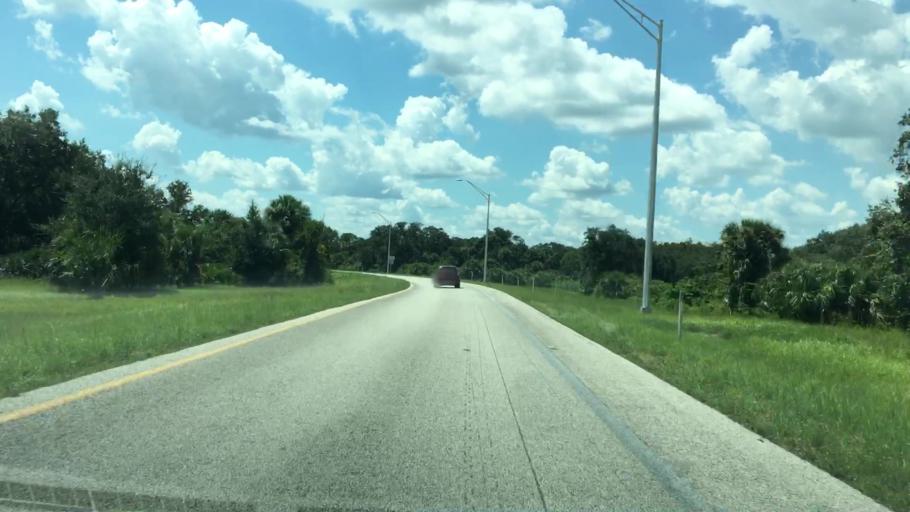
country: US
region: Florida
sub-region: Brevard County
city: South Patrick Shores
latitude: 28.1953
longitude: -80.7106
